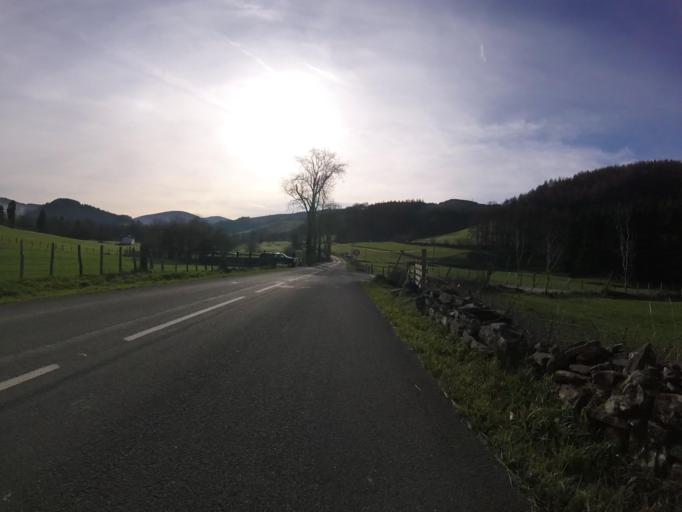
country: ES
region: Basque Country
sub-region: Provincia de Guipuzcoa
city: Berastegui
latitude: 43.1119
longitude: -1.9650
